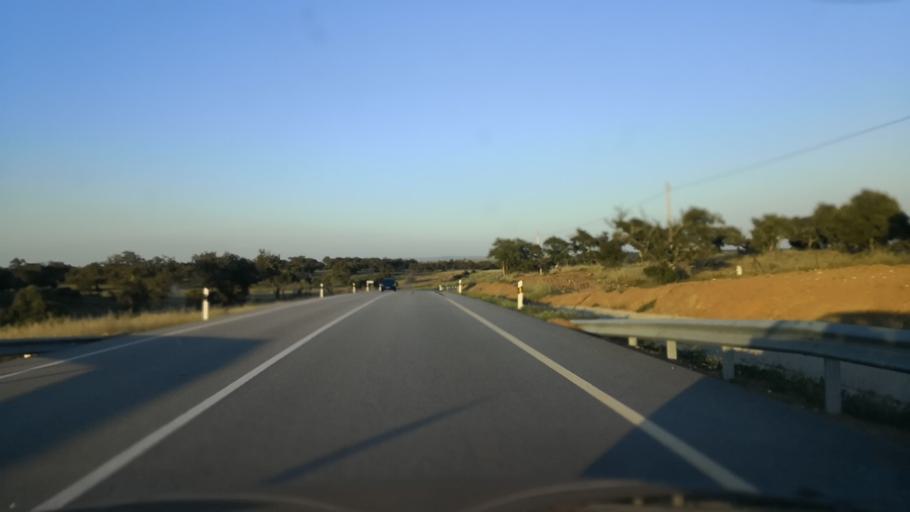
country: ES
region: Extremadura
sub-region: Provincia de Caceres
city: Salorino
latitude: 39.5104
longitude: -7.1097
